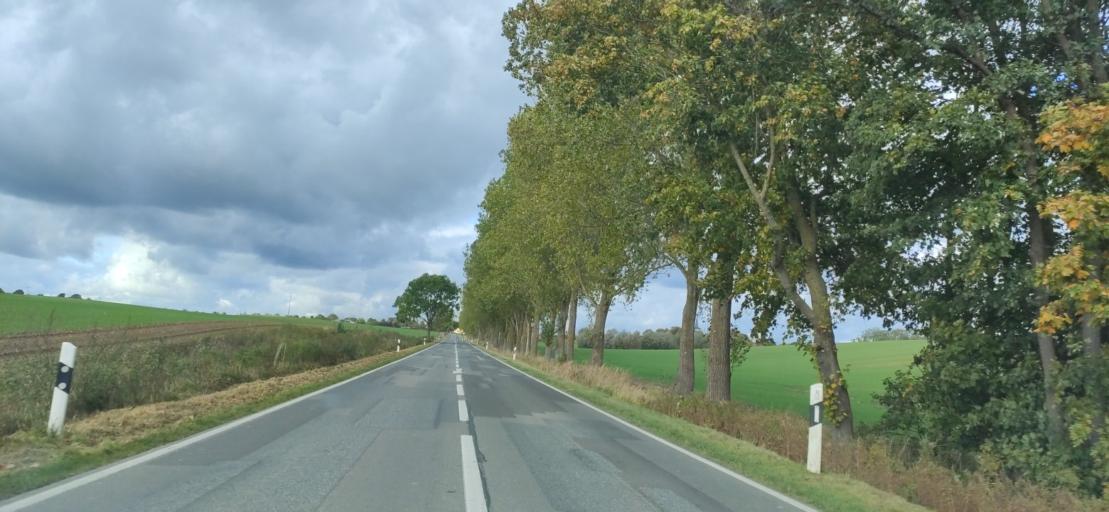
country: DE
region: Mecklenburg-Vorpommern
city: Gross Wokern
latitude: 53.7126
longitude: 12.5466
